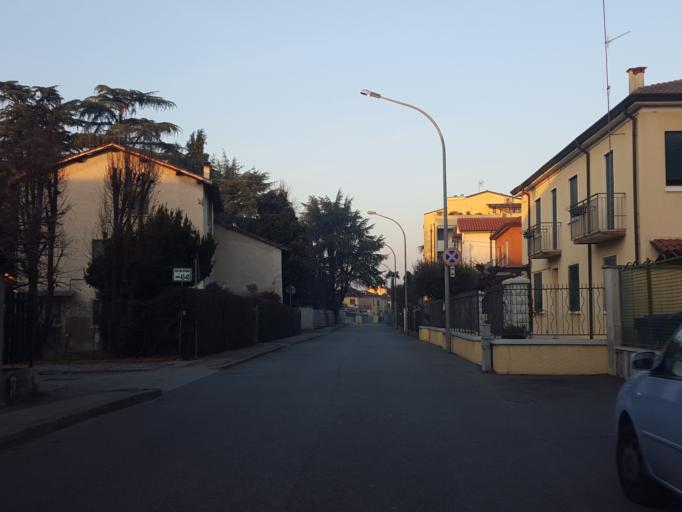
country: IT
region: Veneto
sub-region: Provincia di Vicenza
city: Vicenza
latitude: 45.5610
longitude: 11.5529
